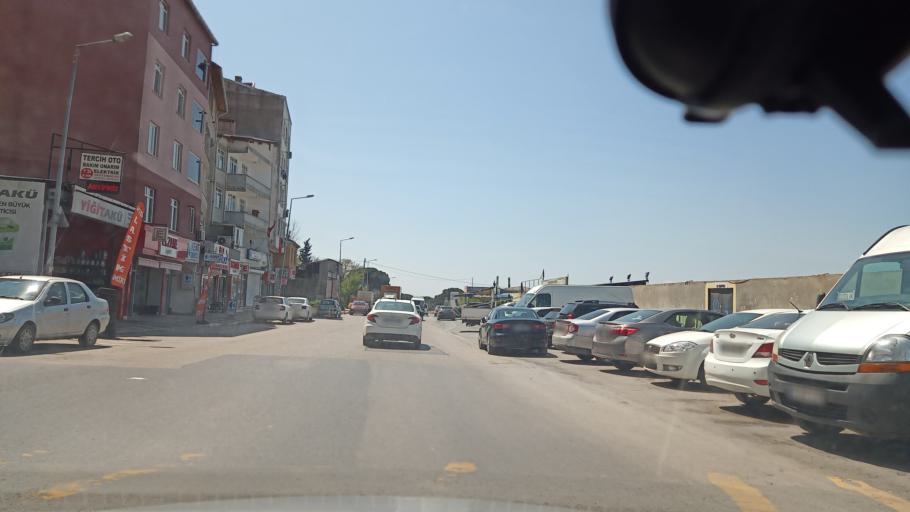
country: TR
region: Istanbul
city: Maltepe
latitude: 40.9545
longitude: 29.1440
